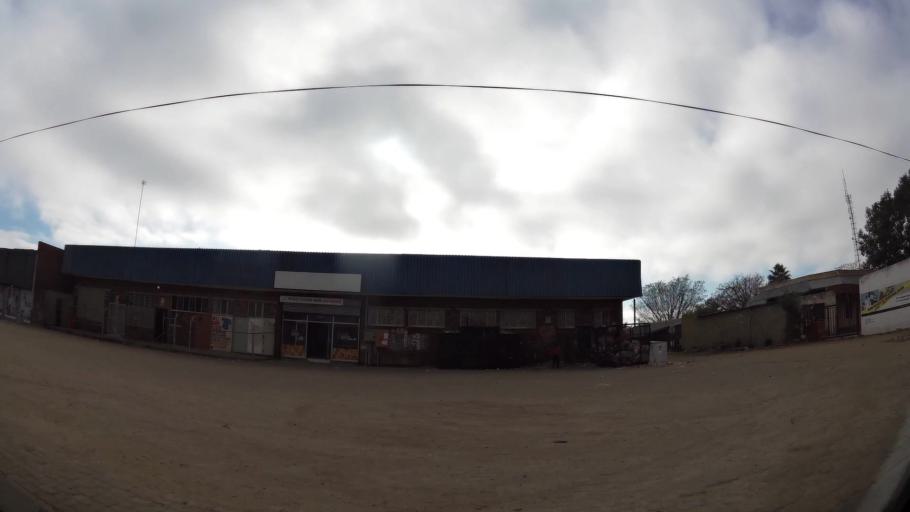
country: ZA
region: Limpopo
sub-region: Capricorn District Municipality
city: Polokwane
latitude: -23.8416
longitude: 29.3857
